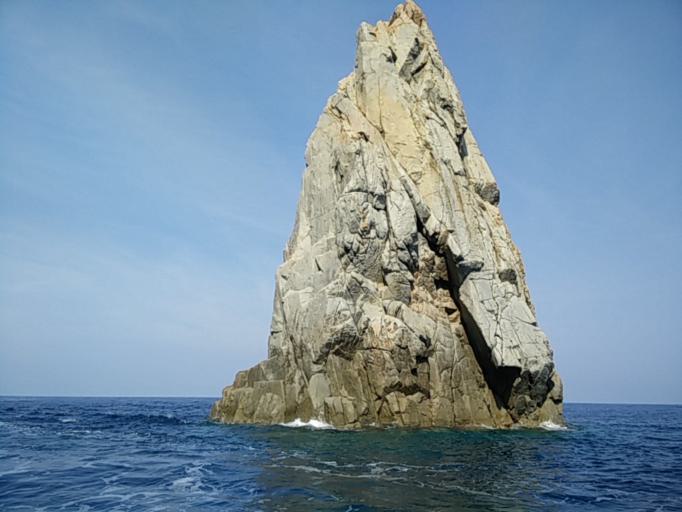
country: FR
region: Corsica
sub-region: Departement de la Corse-du-Sud
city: Cargese
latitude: 42.2396
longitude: 8.5451
